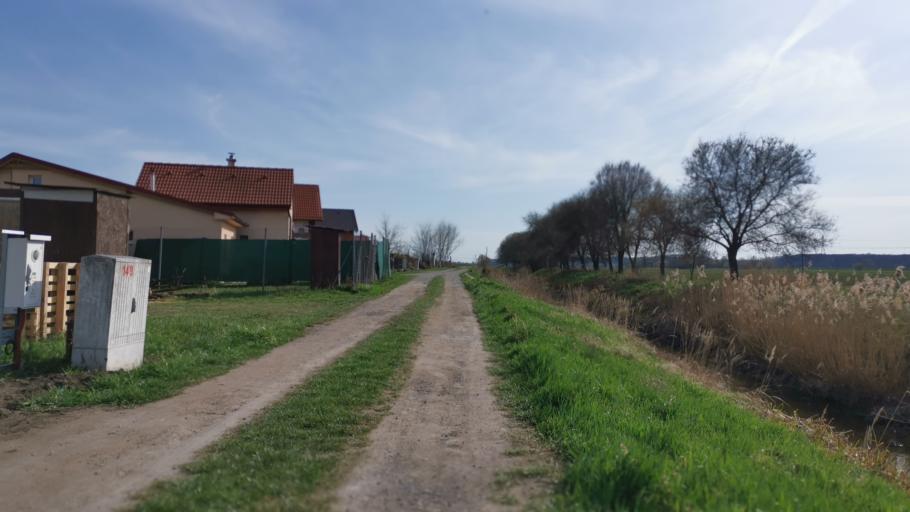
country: CZ
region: South Moravian
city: Tvrdonice
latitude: 48.7265
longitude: 17.0220
